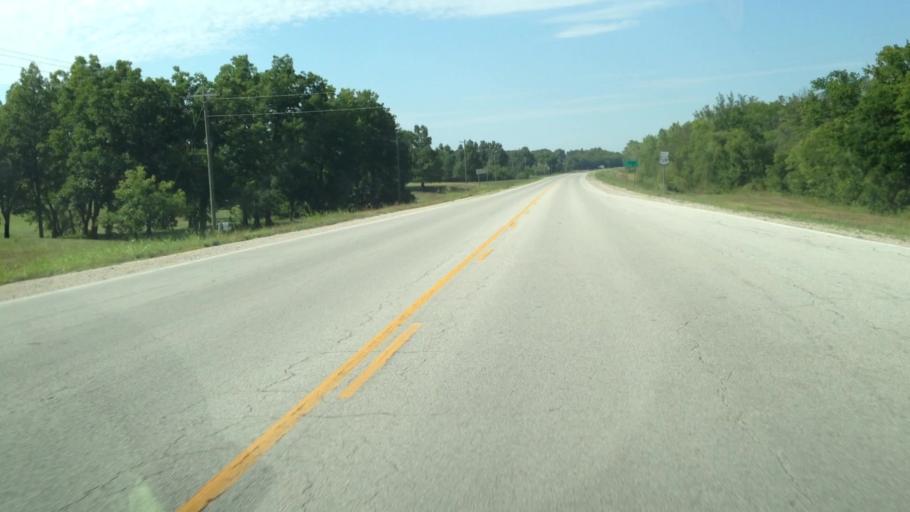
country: US
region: Kansas
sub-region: Neosho County
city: Erie
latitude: 37.5293
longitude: -95.2703
